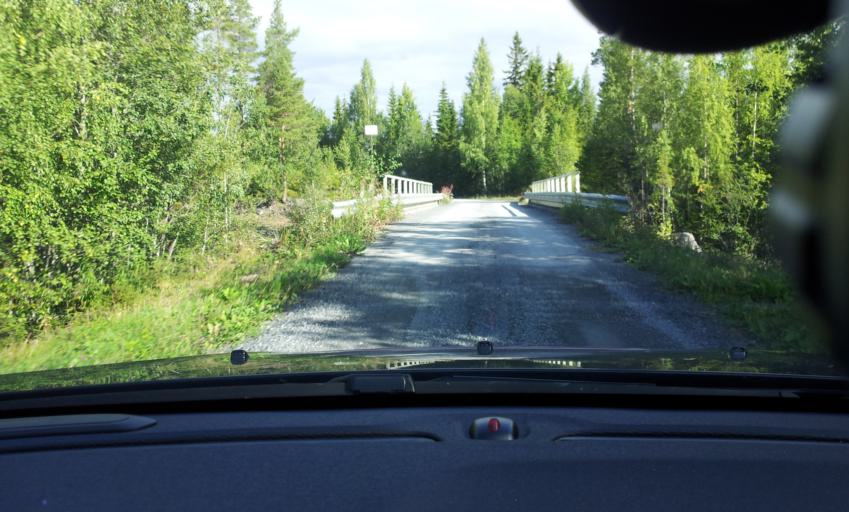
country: SE
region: Jaemtland
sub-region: Krokoms Kommun
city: Valla
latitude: 63.2640
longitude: 13.7878
